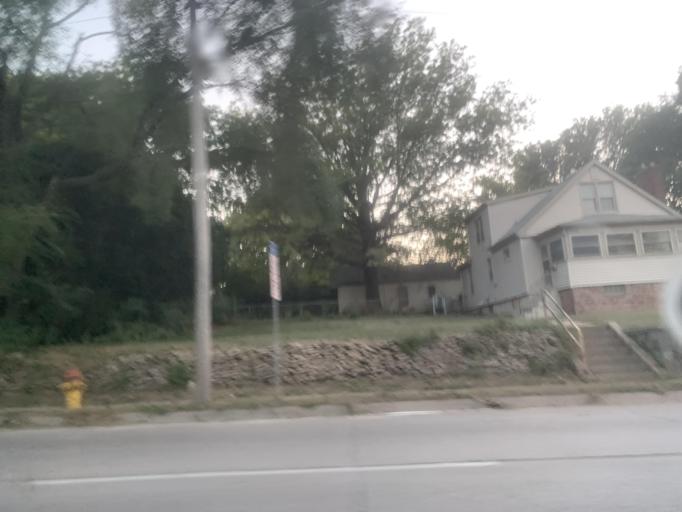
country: US
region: Nebraska
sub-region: Douglas County
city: Omaha
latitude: 41.2187
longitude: -95.9760
